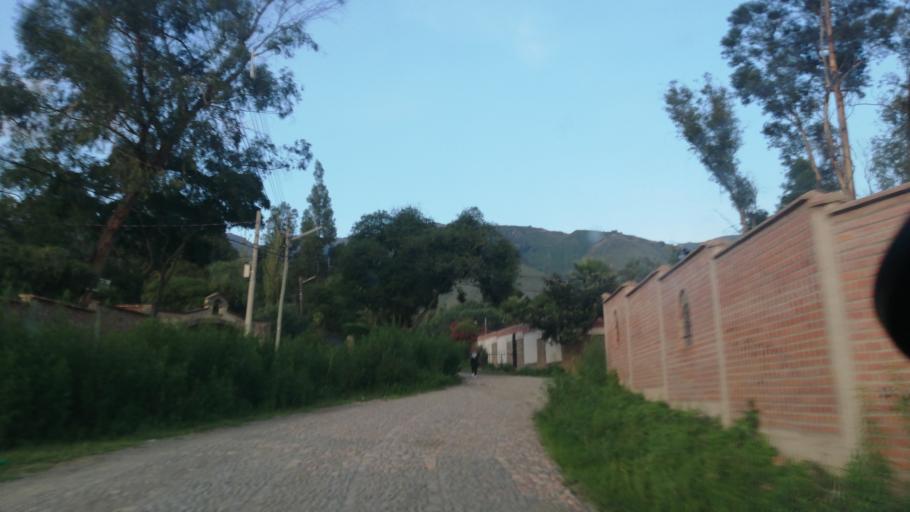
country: BO
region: Cochabamba
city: Cochabamba
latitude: -17.3353
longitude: -66.2097
